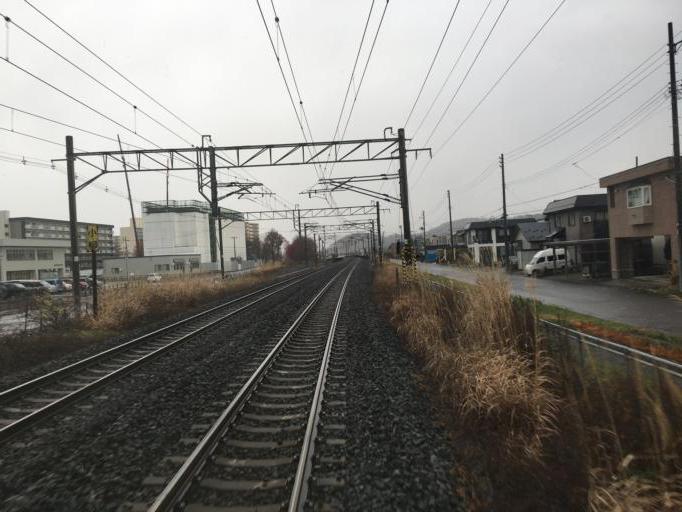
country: JP
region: Aomori
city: Aomori Shi
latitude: 40.8169
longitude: 140.7955
